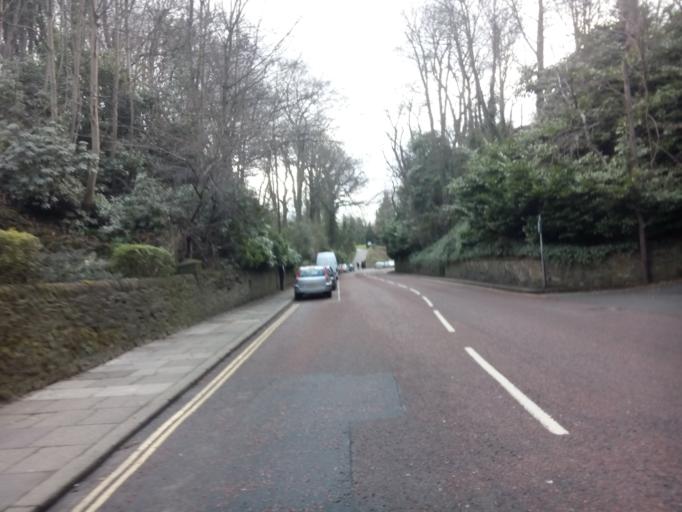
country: GB
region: England
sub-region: County Durham
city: Durham
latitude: 54.7811
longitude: -1.5853
